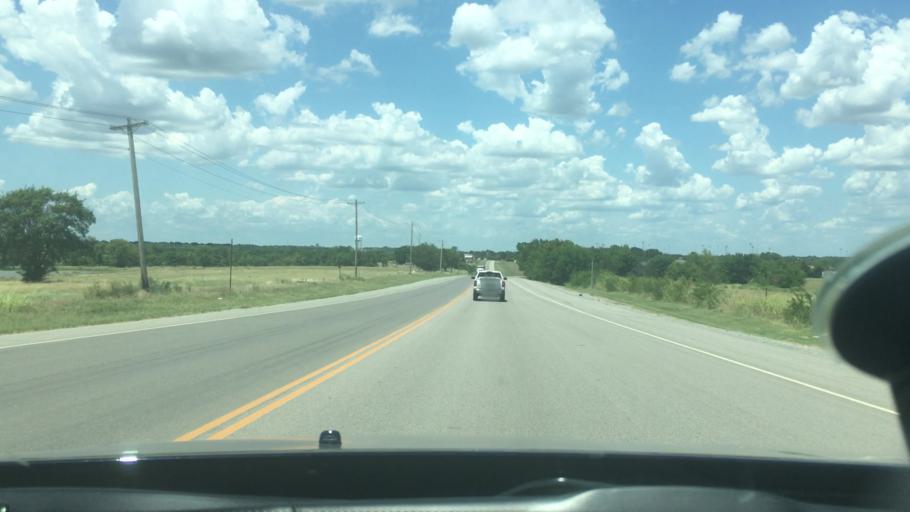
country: US
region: Oklahoma
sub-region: Bryan County
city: Durant
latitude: 33.9689
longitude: -96.3731
